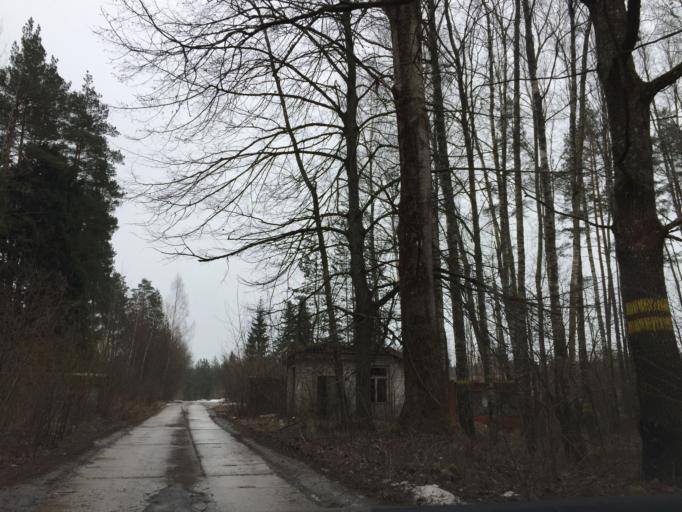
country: LV
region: Lecava
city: Iecava
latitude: 56.5981
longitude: 24.0719
